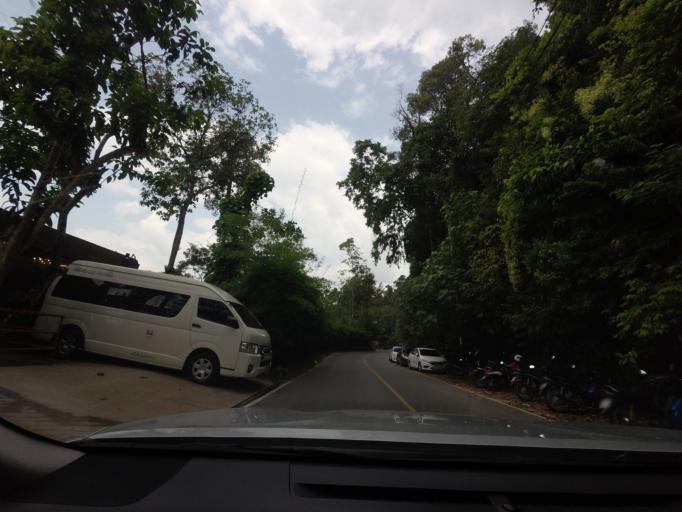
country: TH
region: Phangnga
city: Ban Ao Nang
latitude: 8.0908
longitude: 98.7480
